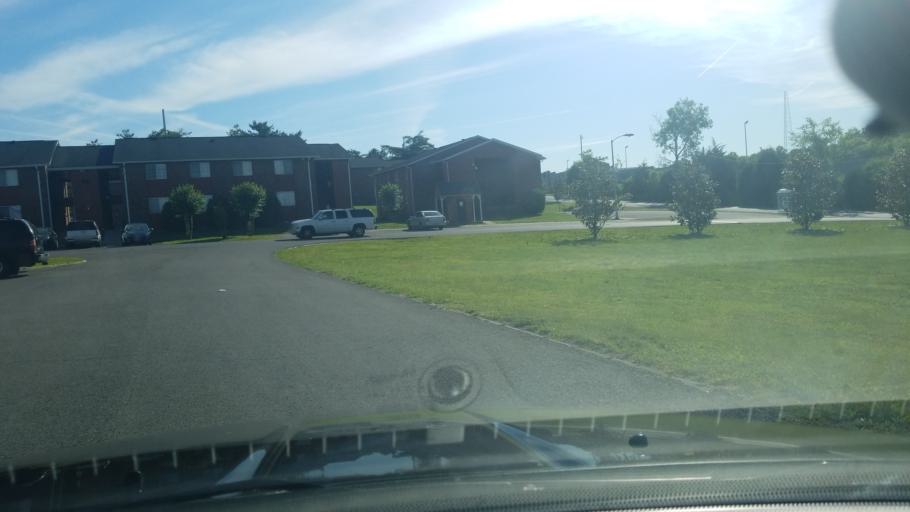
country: US
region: Tennessee
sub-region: Davidson County
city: Nashville
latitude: 36.2336
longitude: -86.7694
